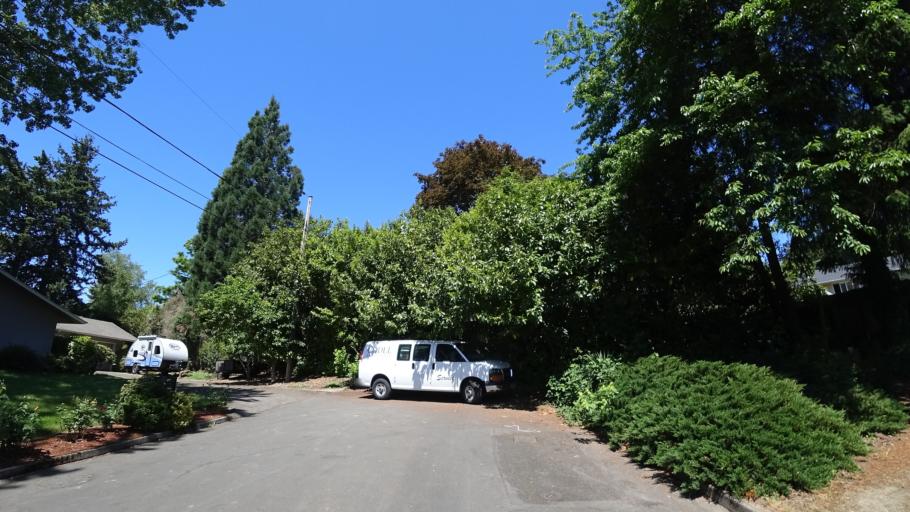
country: US
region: Oregon
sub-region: Multnomah County
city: Portland
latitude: 45.4846
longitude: -122.7101
